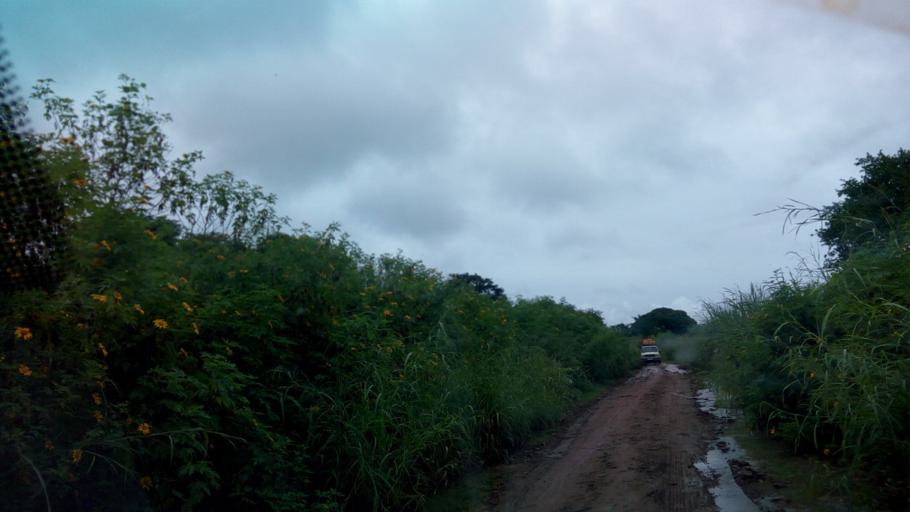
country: ZM
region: Luapula
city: Nchelenge
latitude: -9.0900
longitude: 28.3312
